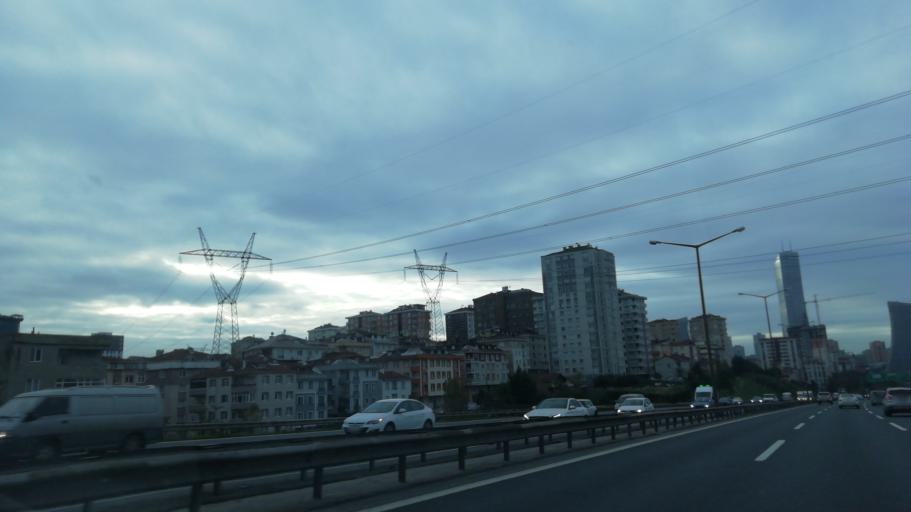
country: TR
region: Istanbul
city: Umraniye
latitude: 41.0093
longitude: 29.1218
